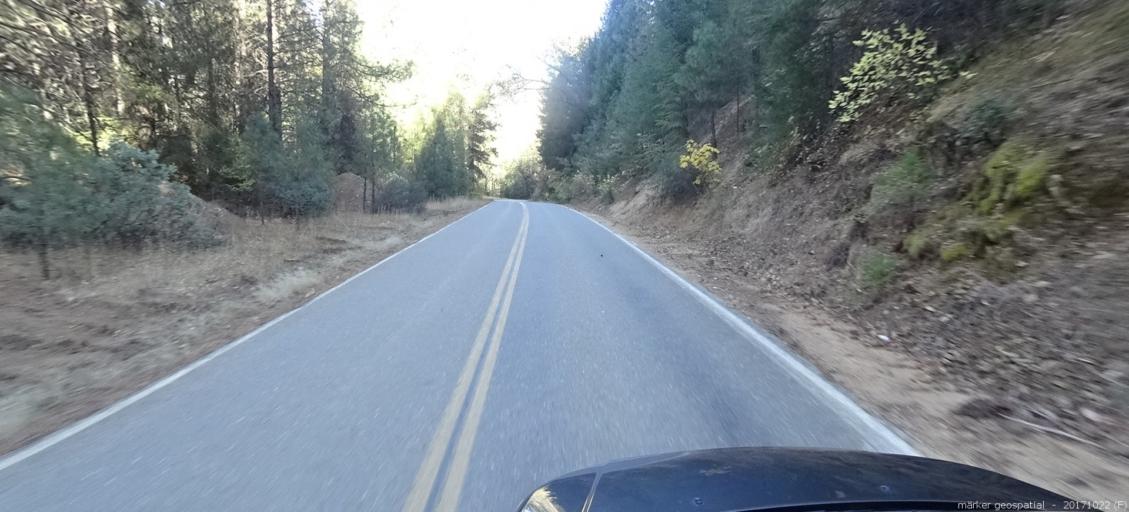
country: US
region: California
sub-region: Shasta County
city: Shasta Lake
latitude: 40.9112
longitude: -122.2421
